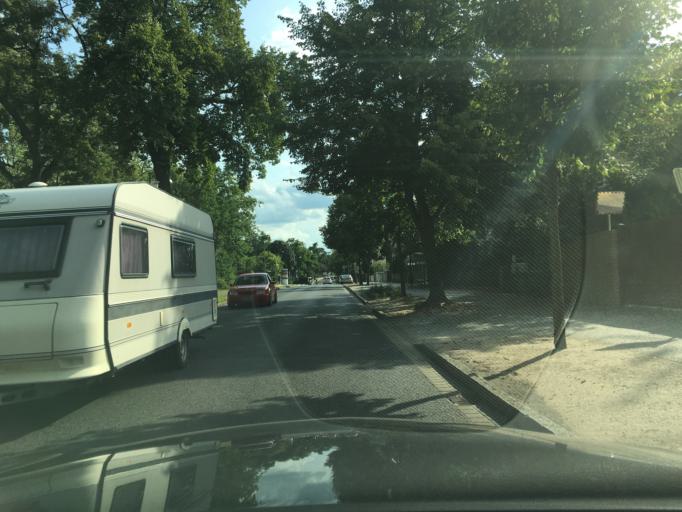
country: DE
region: Mecklenburg-Vorpommern
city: Neustrelitz
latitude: 53.3701
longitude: 13.0714
